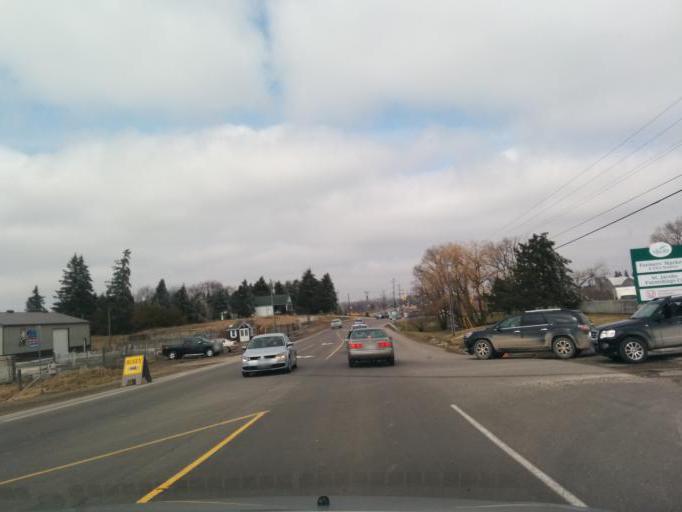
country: CA
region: Ontario
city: Waterloo
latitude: 43.5122
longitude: -80.5571
